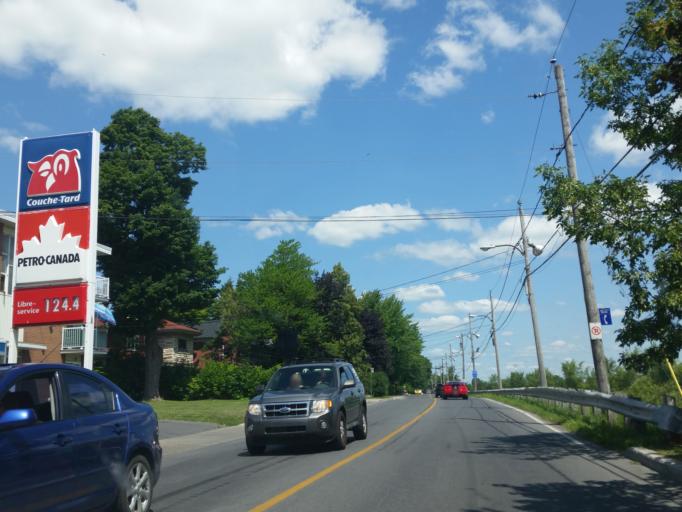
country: CA
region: Quebec
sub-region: Monteregie
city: Saint-Jean-sur-Richelieu
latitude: 45.3115
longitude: -73.2521
